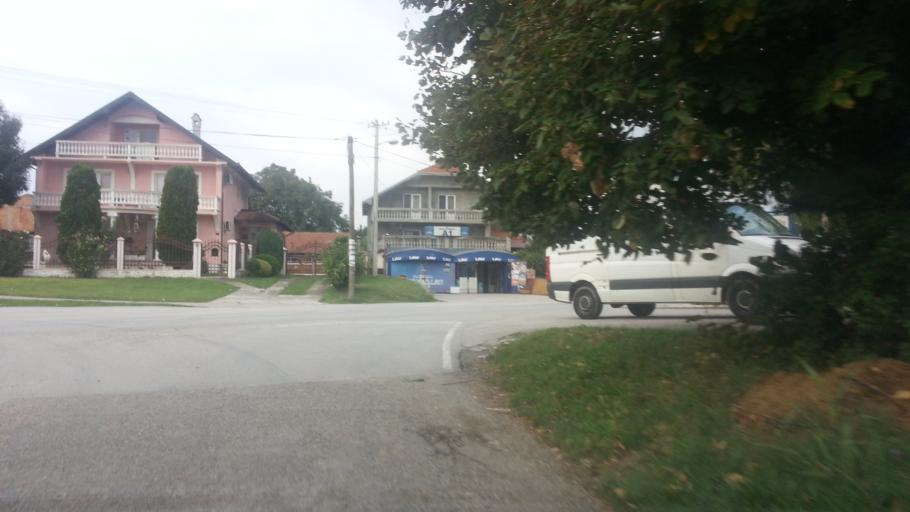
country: RS
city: Stari Banovci
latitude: 44.9807
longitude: 20.2777
